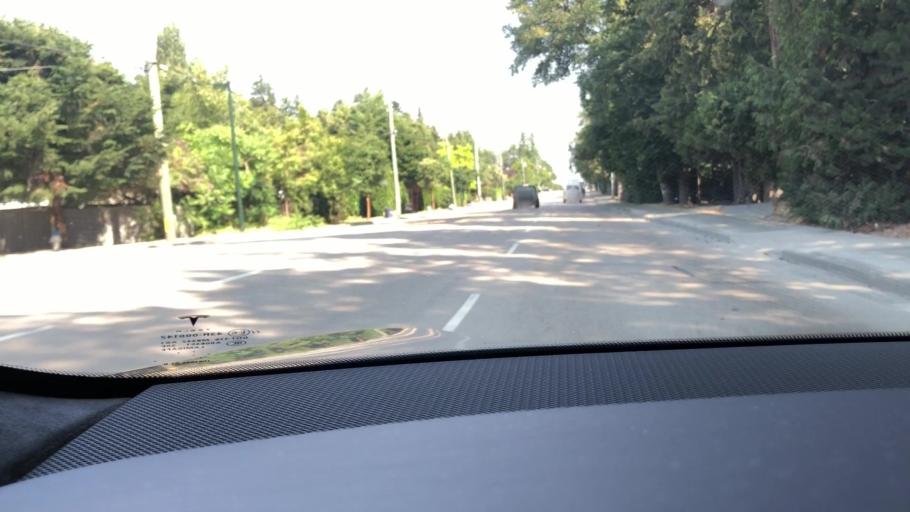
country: US
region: Washington
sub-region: Whatcom County
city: Point Roberts
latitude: 49.0150
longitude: -123.0685
